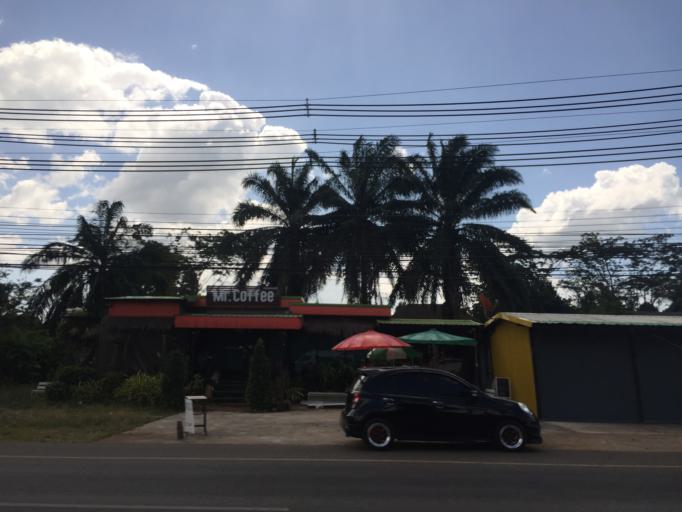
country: TH
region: Krabi
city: Krabi
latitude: 8.0828
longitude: 98.8637
